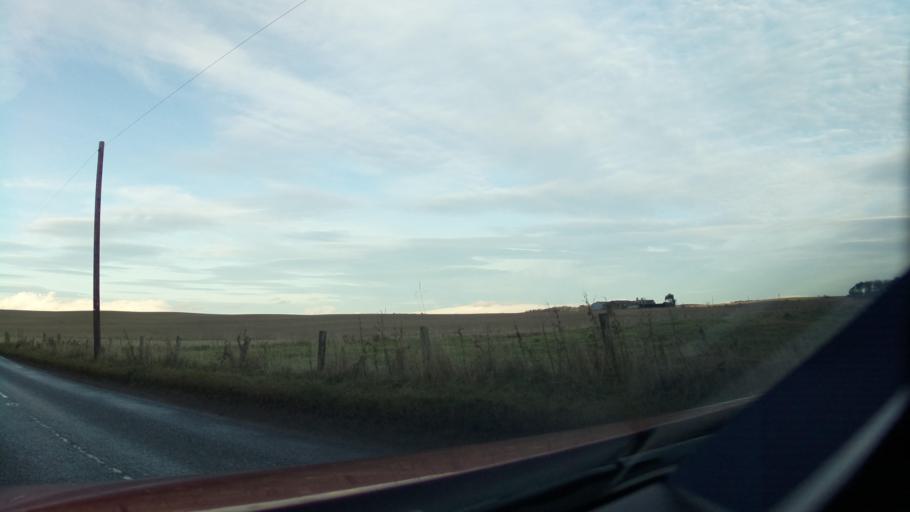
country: GB
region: Scotland
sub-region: Angus
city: Letham
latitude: 56.5686
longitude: -2.7777
